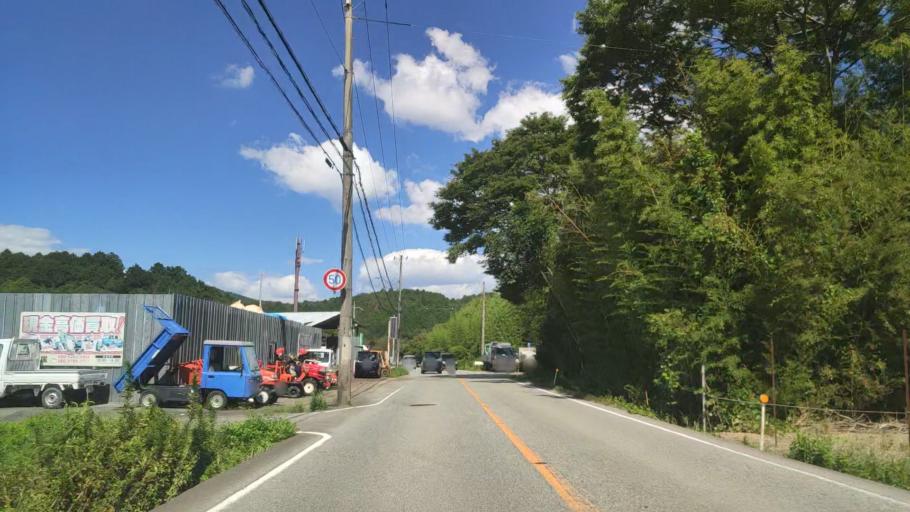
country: JP
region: Kyoto
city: Fukuchiyama
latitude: 35.1844
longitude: 135.1239
